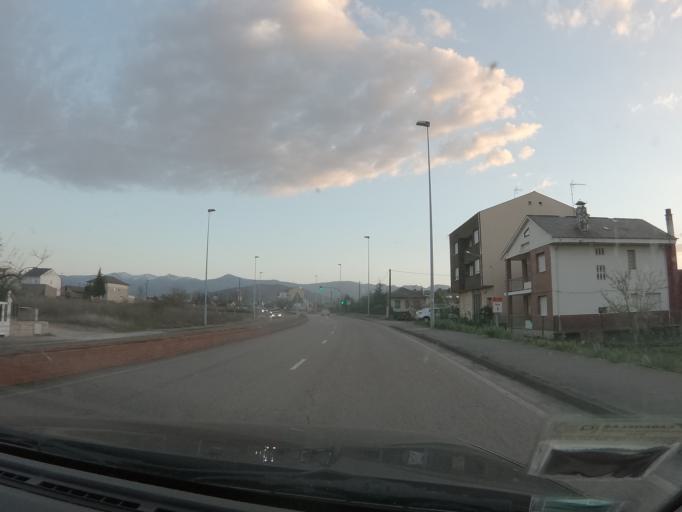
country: ES
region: Castille and Leon
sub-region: Provincia de Leon
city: Ponferrada
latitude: 42.5773
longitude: -6.6097
